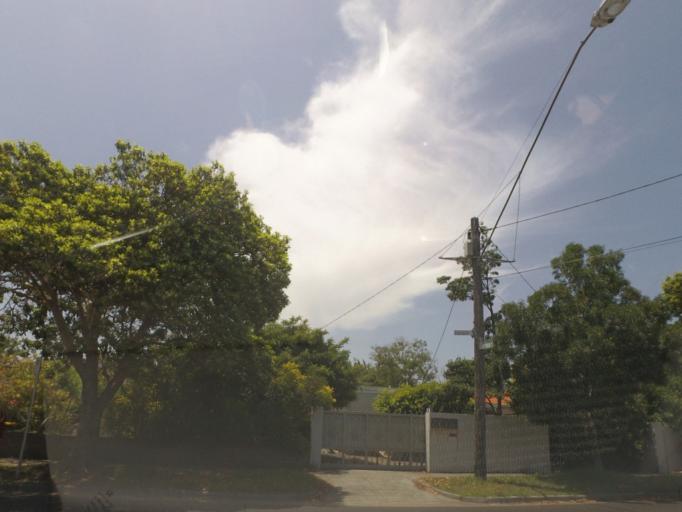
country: AU
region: Victoria
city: McKinnon
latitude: -37.9273
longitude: 145.0496
